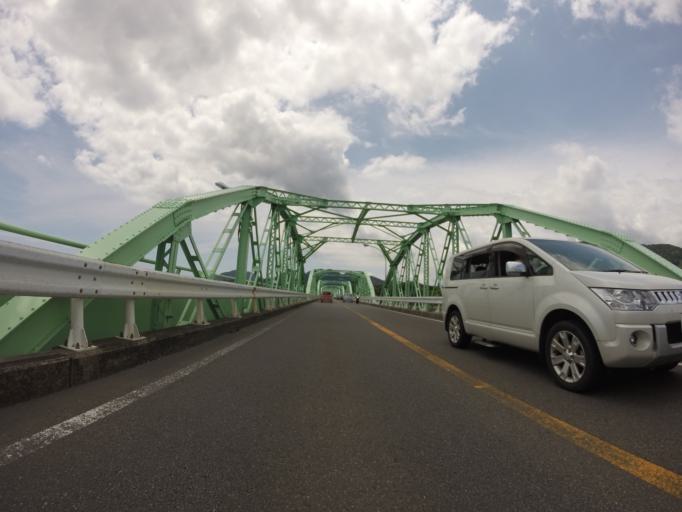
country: JP
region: Shizuoka
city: Shizuoka-shi
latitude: 34.9610
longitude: 138.3687
